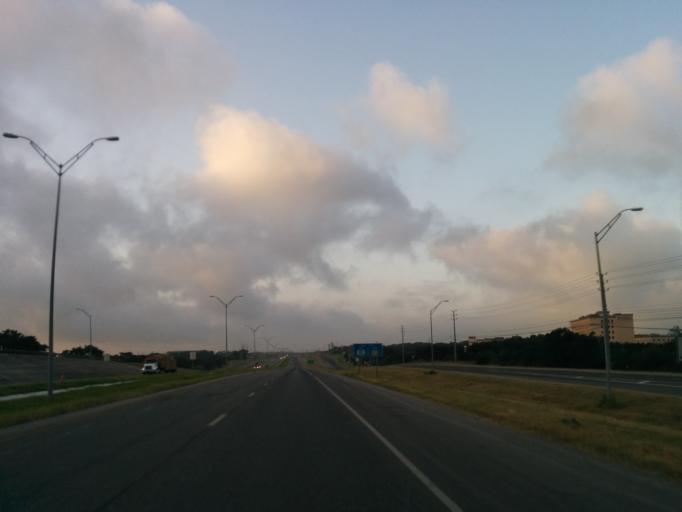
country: US
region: Texas
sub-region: Bexar County
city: Leon Valley
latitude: 29.4722
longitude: -98.6967
